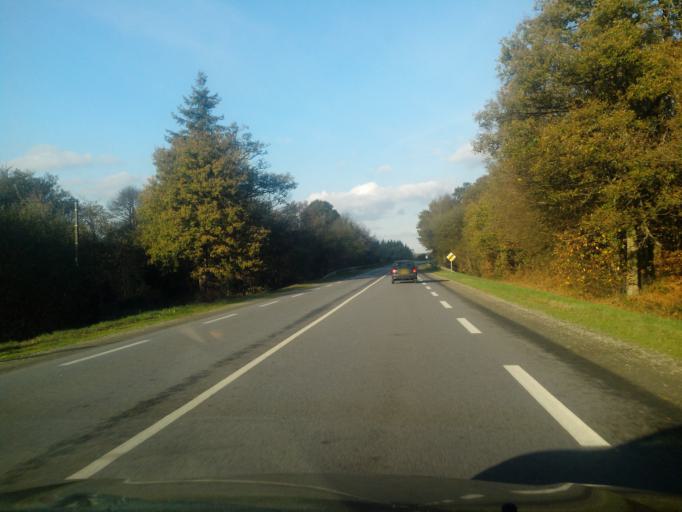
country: FR
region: Brittany
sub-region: Departement du Morbihan
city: Loyat
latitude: 47.9707
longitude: -2.3825
